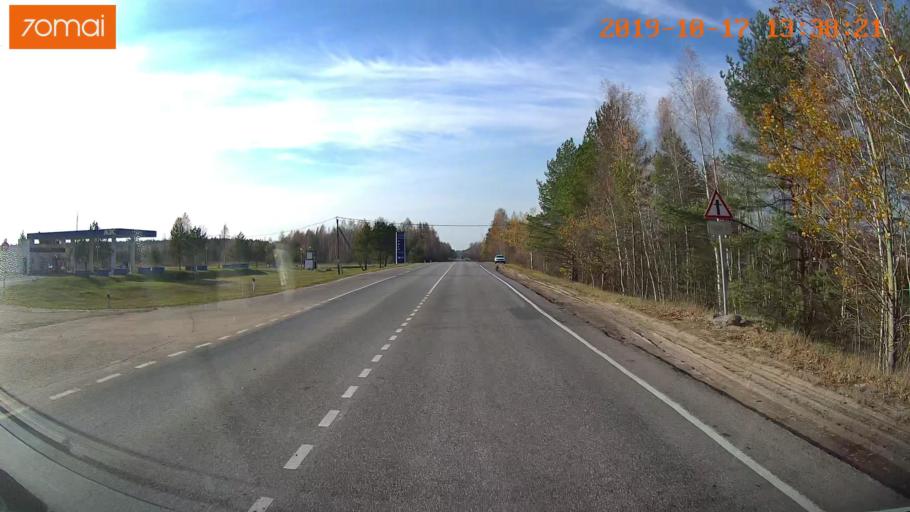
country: RU
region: Rjazan
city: Tuma
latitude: 55.1437
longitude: 40.6158
